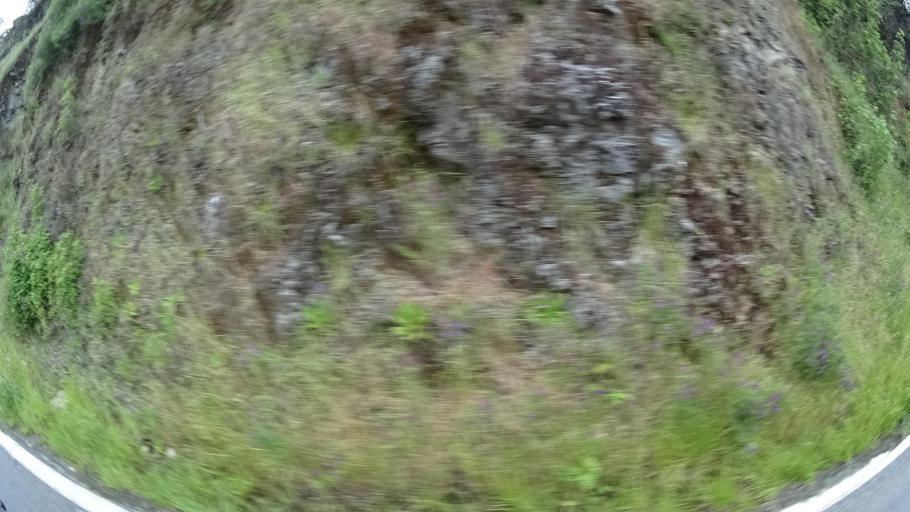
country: US
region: California
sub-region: Humboldt County
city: Willow Creek
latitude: 41.2977
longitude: -123.5526
